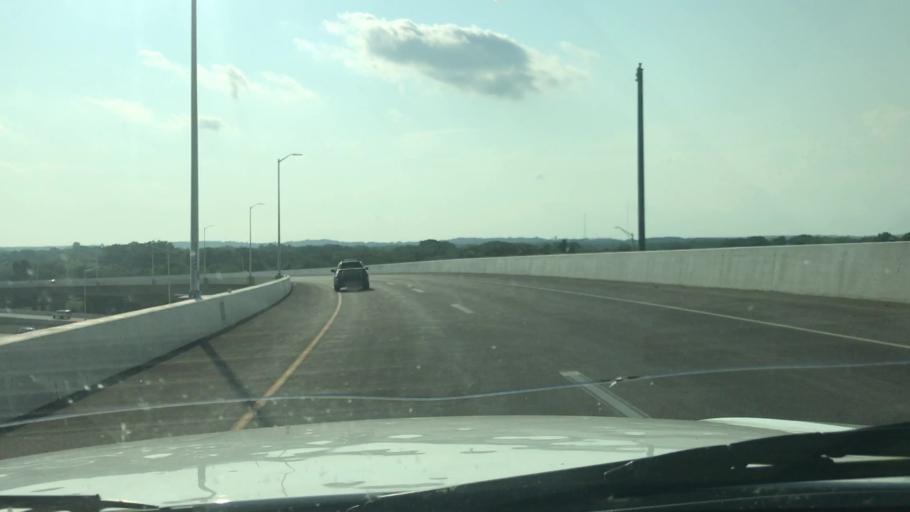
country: US
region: Wisconsin
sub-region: Brown County
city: Howard
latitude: 44.5592
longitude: -88.0498
